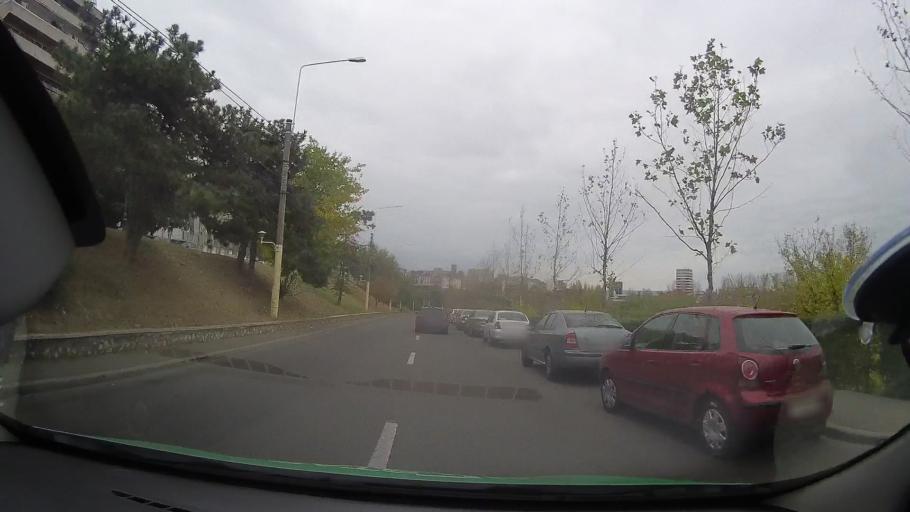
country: RO
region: Constanta
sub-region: Municipiul Constanta
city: Constanta
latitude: 44.1746
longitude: 28.6540
